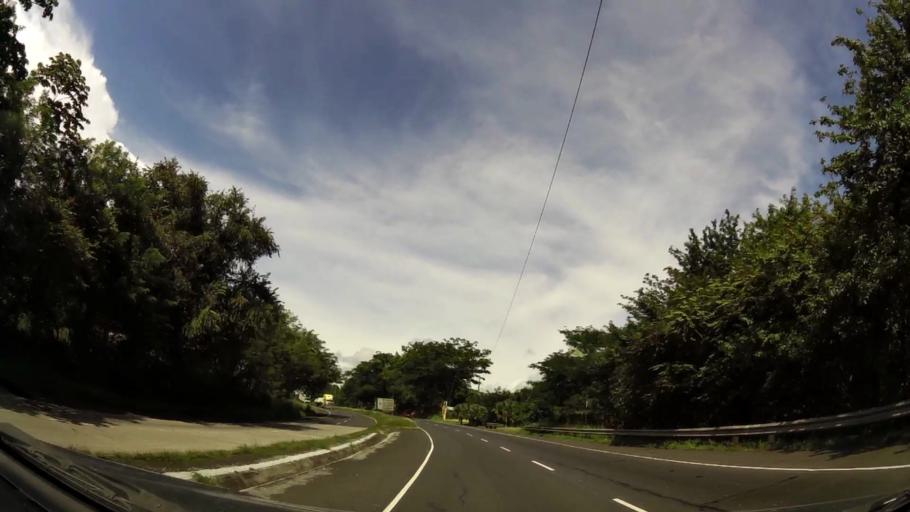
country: PA
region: Panama
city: Capira
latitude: 8.6758
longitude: -79.8686
